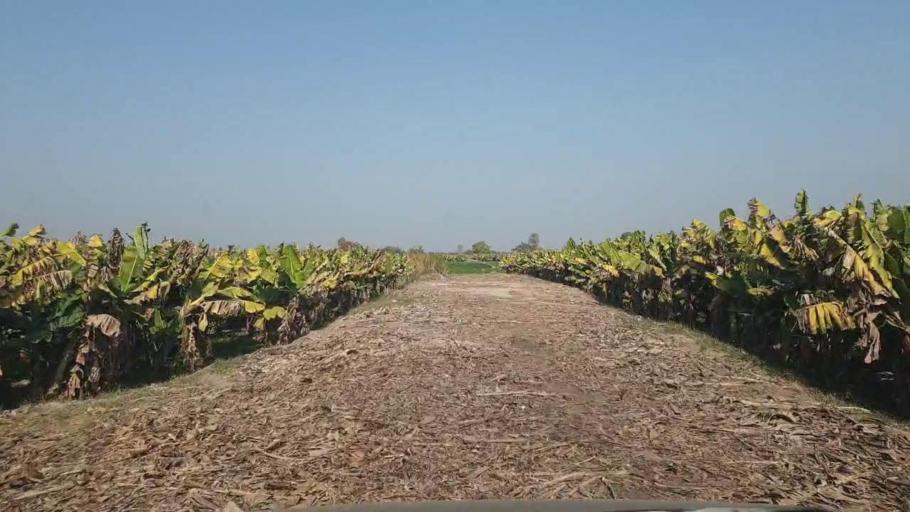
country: PK
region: Sindh
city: Tando Adam
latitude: 25.7701
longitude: 68.5992
